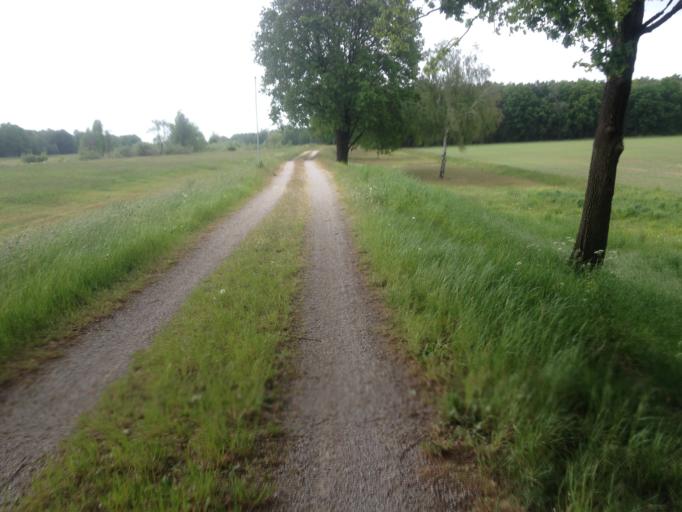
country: DE
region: Brandenburg
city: Drehnow
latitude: 51.8298
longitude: 14.3505
